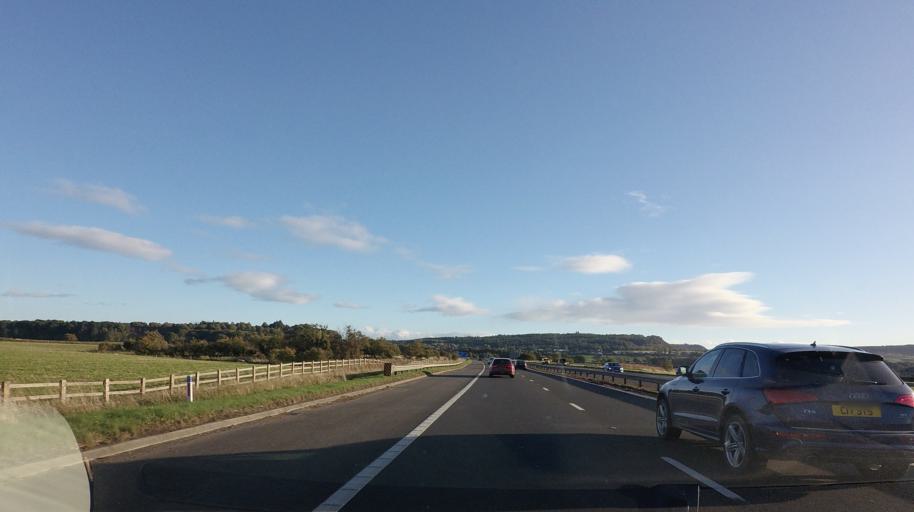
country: GB
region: Scotland
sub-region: Stirling
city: Stirling
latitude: 56.1258
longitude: -3.9708
